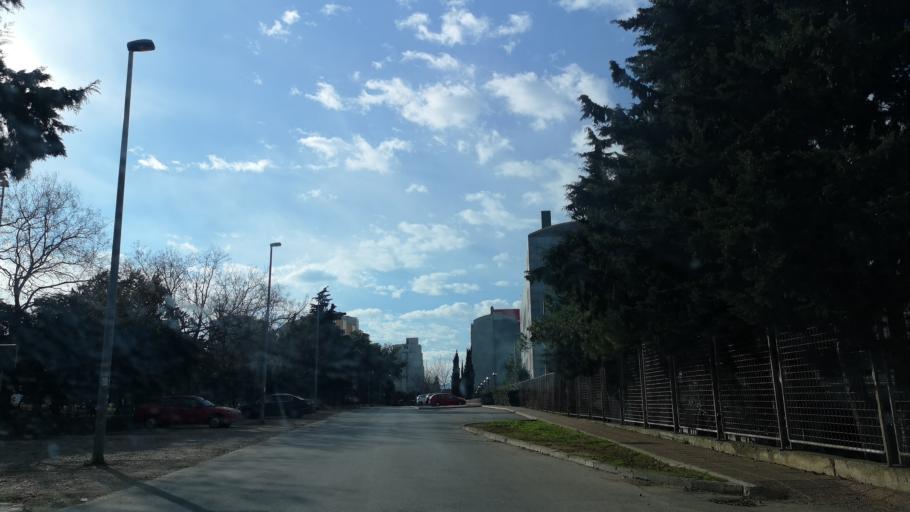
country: HR
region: Zadarska
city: Zadar
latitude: 44.1211
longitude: 15.2420
